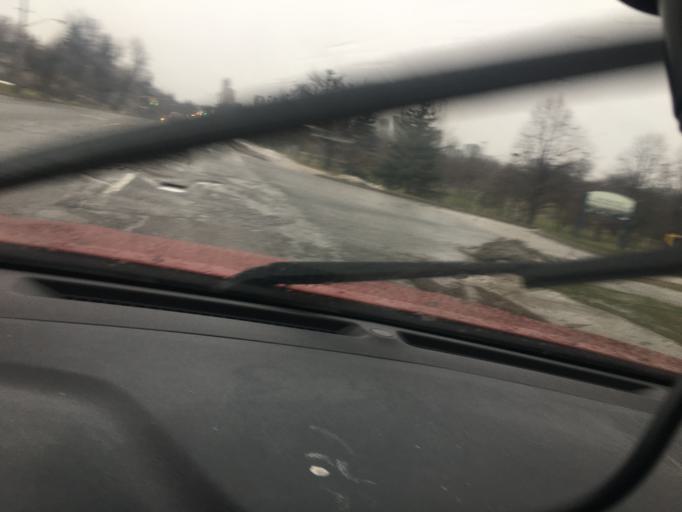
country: CA
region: Ontario
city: Scarborough
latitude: 43.7575
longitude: -79.2565
